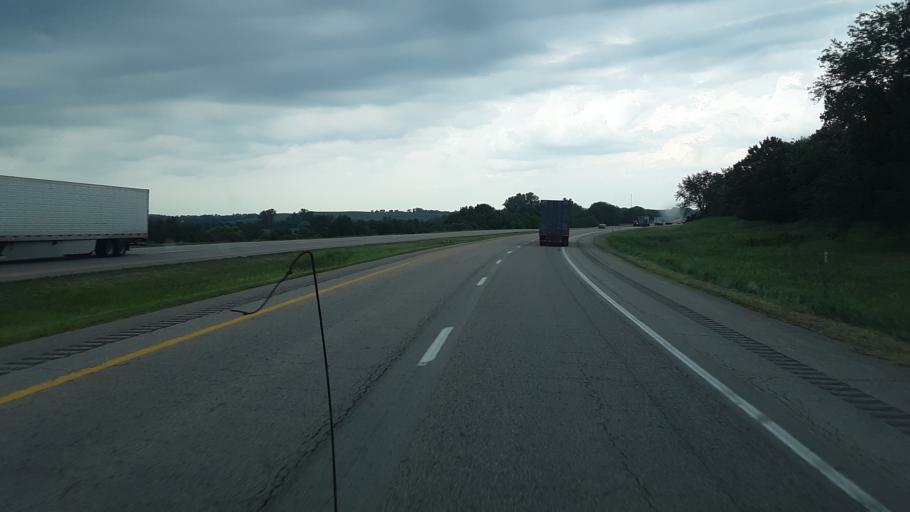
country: US
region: Iowa
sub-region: Pottawattamie County
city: Council Bluffs
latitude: 41.3933
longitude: -95.6671
